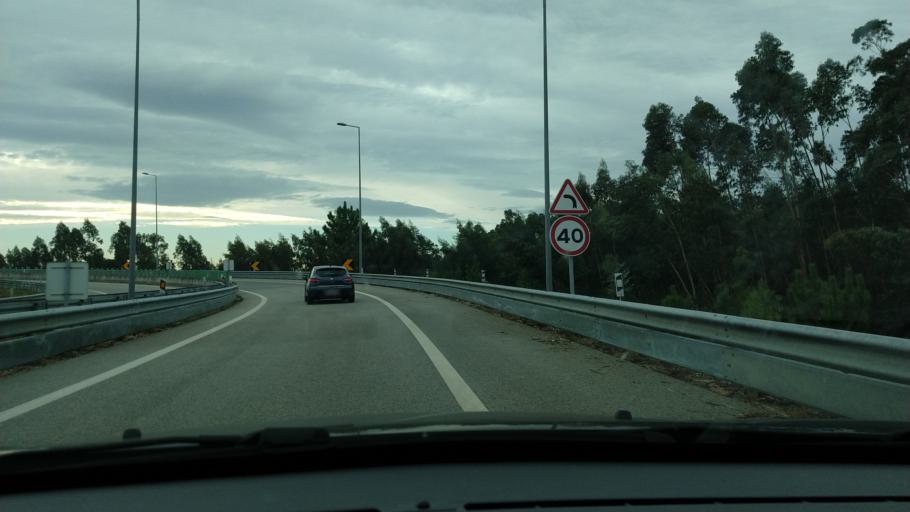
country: PT
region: Coimbra
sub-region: Figueira da Foz
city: Alhadas
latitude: 40.1526
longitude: -8.7840
